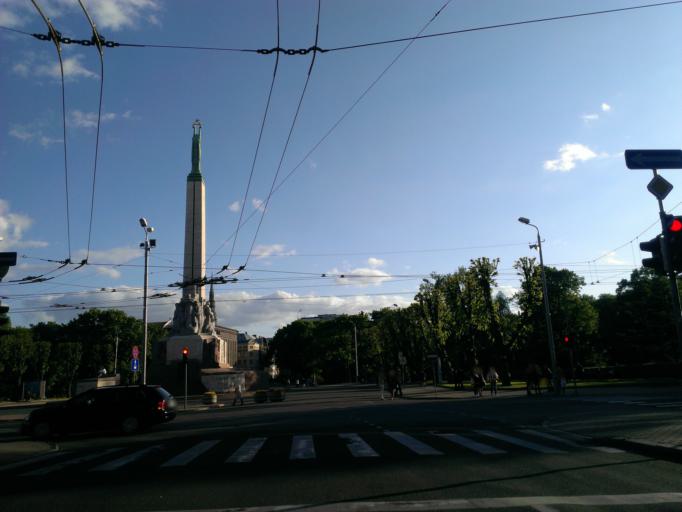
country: LV
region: Riga
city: Riga
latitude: 56.9522
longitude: 24.1140
